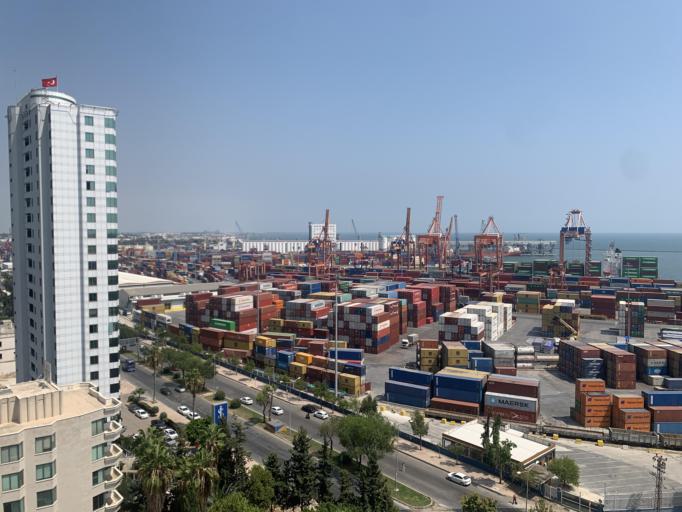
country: TR
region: Mersin
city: Mercin
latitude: 36.8042
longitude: 34.6373
